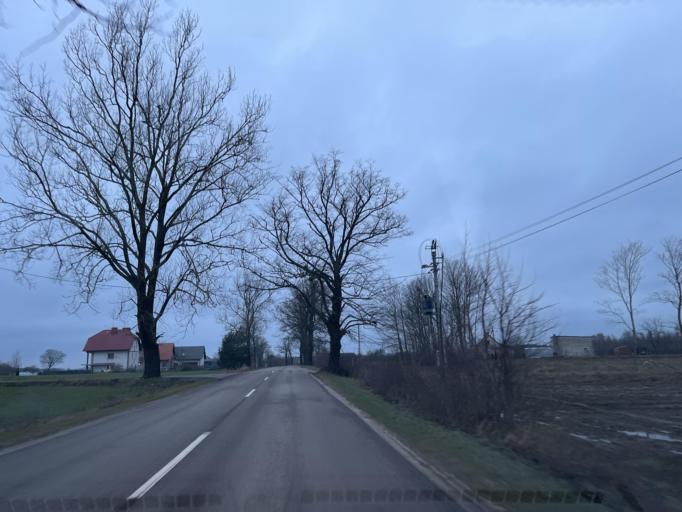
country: PL
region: Pomeranian Voivodeship
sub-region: Powiat kartuski
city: Kartuzy
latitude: 54.4082
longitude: 18.2120
